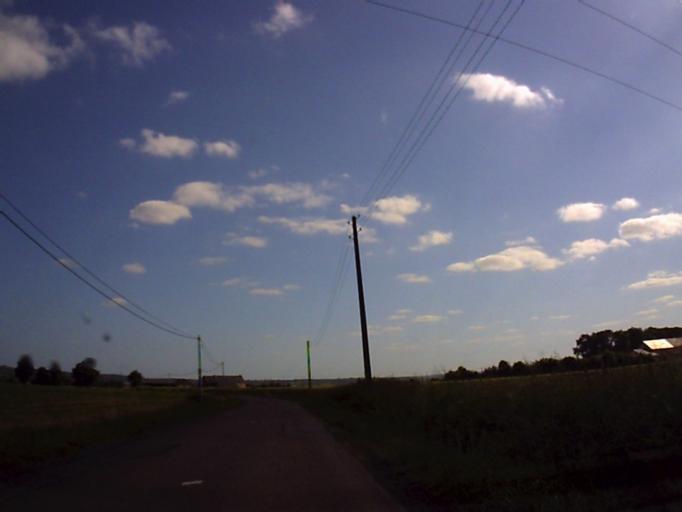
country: FR
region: Brittany
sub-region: Departement d'Ille-et-Vilaine
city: Iffendic
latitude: 48.1511
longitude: -2.0150
